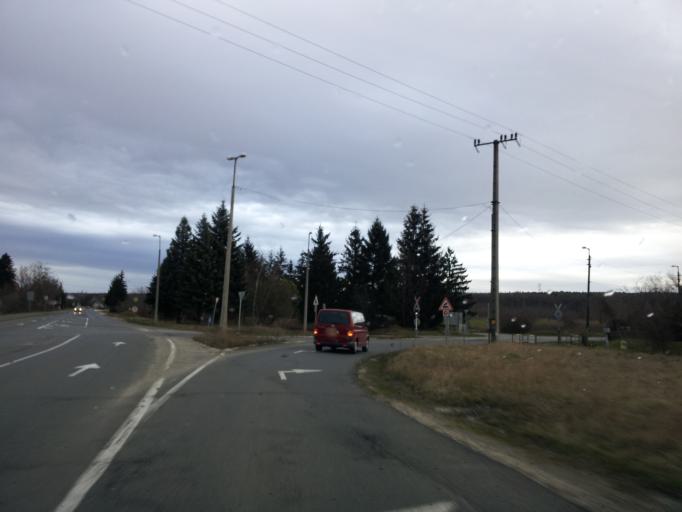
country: HU
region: Vas
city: Koszeg
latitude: 47.3841
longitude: 16.5545
